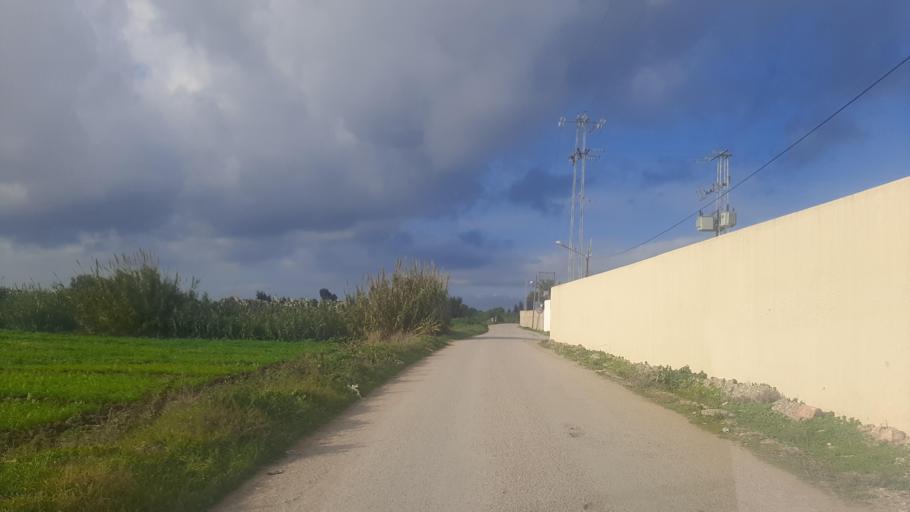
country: TN
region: Nabul
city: Manzil Bu Zalafah
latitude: 36.7075
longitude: 10.5026
